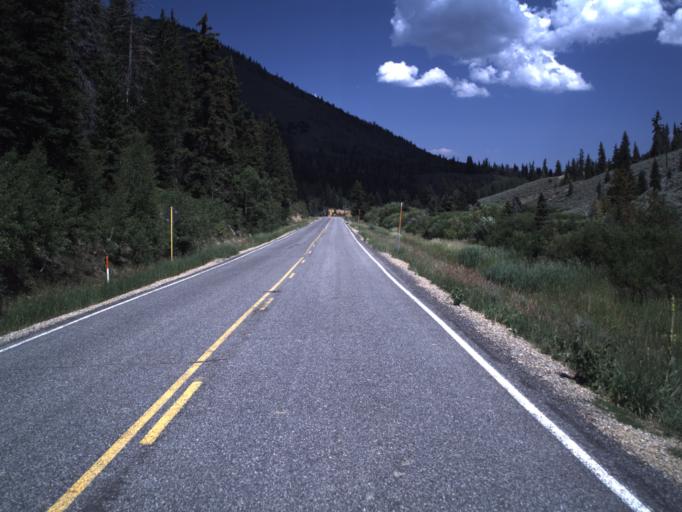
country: US
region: Utah
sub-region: Sanpete County
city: Fairview
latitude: 39.6746
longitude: -111.1557
